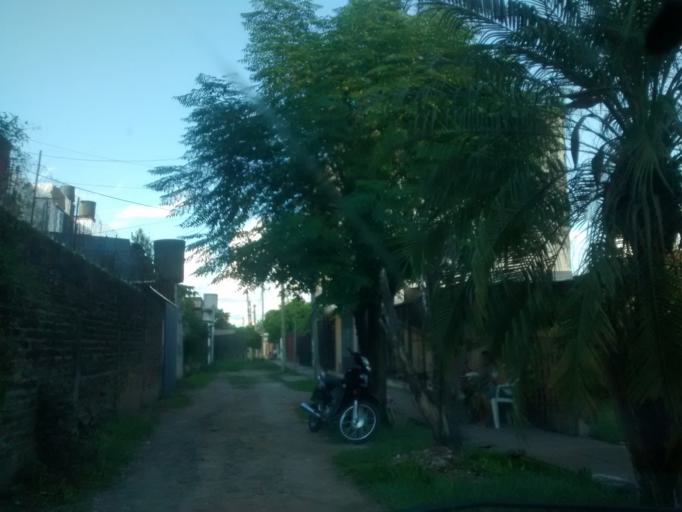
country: AR
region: Chaco
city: Resistencia
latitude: -27.4496
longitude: -59.0143
